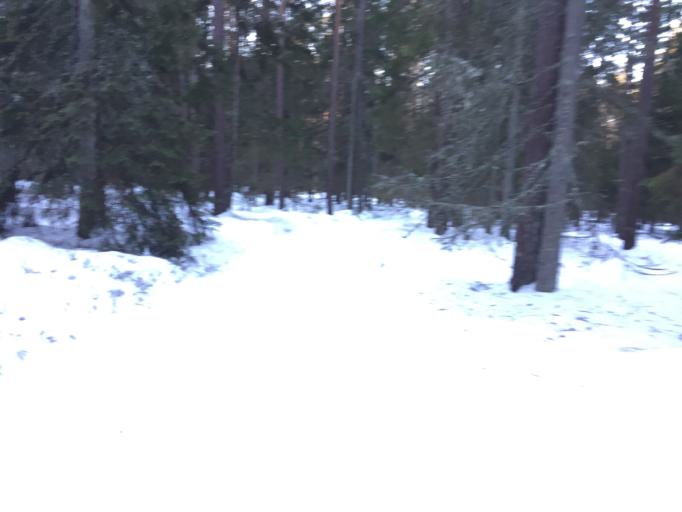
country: LV
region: Kegums
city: Kegums
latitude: 56.7325
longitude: 24.6458
